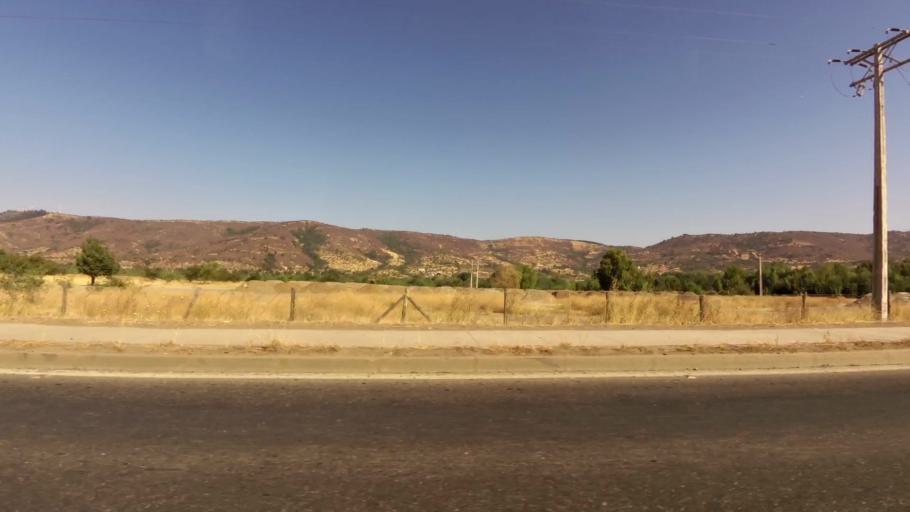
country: CL
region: Maule
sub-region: Provincia de Talca
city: Talca
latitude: -35.4059
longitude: -71.6652
